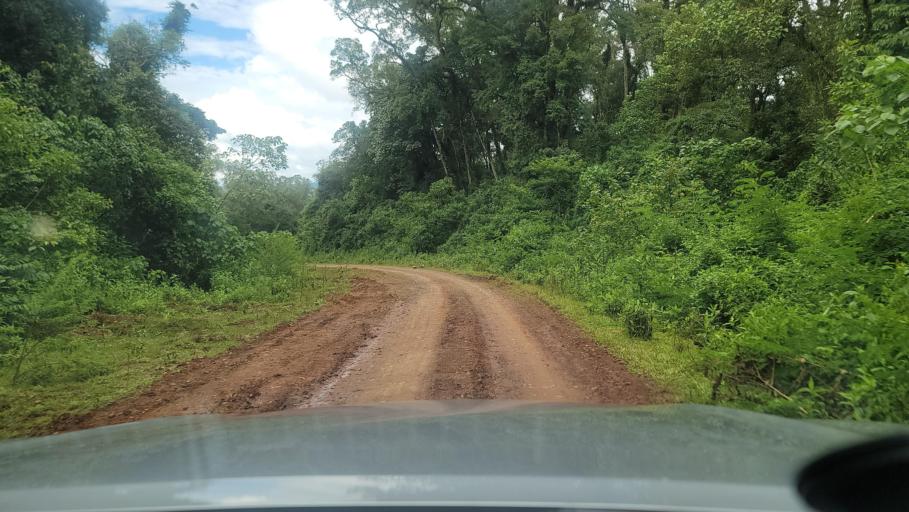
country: ET
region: Southern Nations, Nationalities, and People's Region
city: Bonga
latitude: 7.6241
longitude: 36.2105
